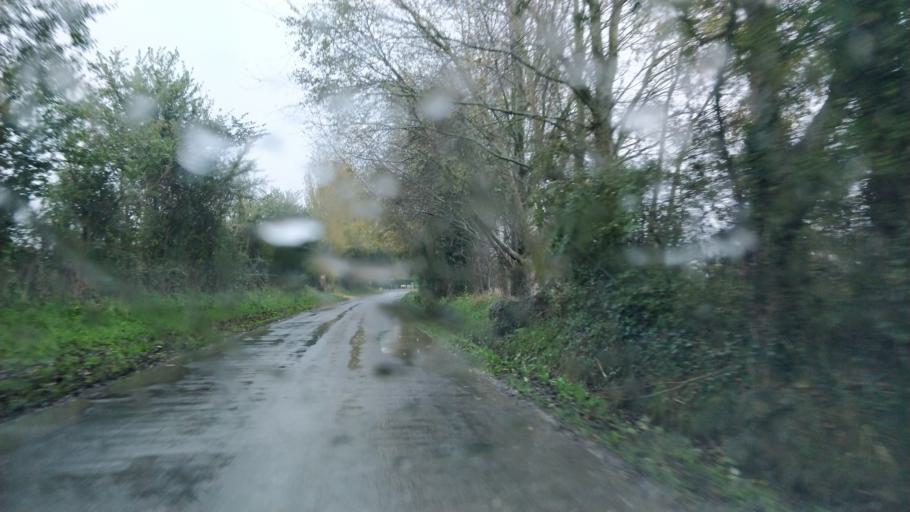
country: FR
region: Lower Normandy
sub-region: Departement de la Manche
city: Brehal
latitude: 48.9021
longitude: -1.5472
